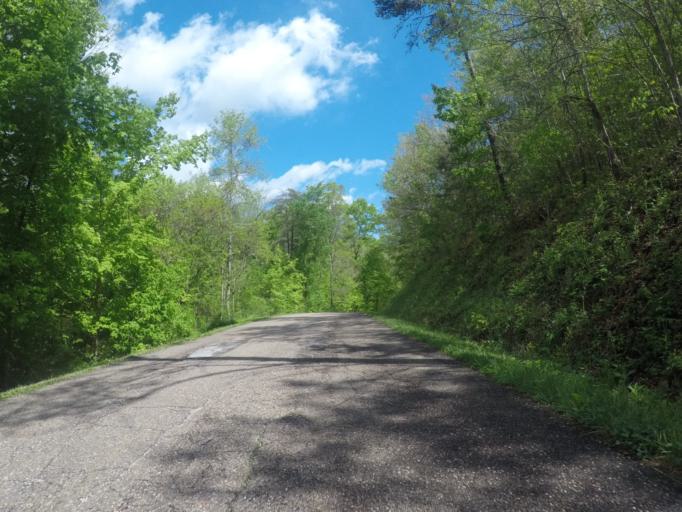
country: US
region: West Virginia
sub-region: Cabell County
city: Huntington
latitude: 38.5379
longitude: -82.4405
